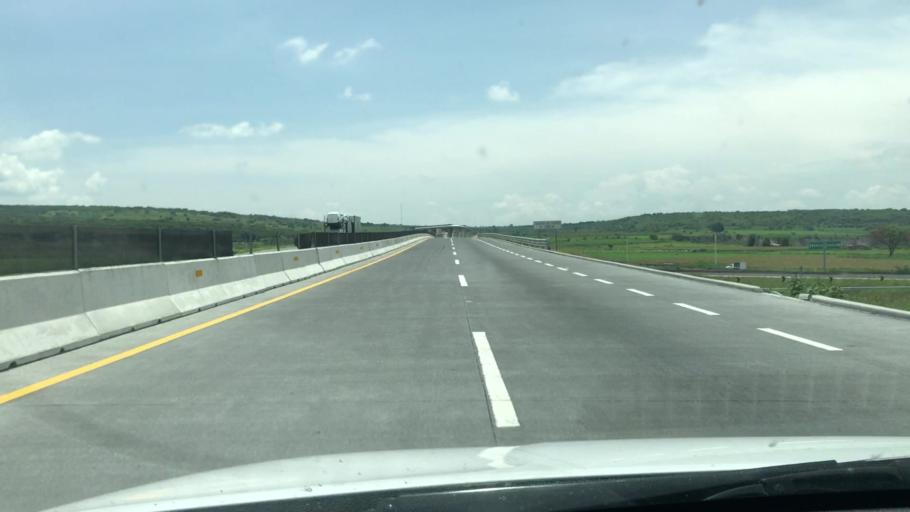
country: MX
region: Guanajuato
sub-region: Penjamo
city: Estacion la Piedad
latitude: 20.3967
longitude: -101.9980
